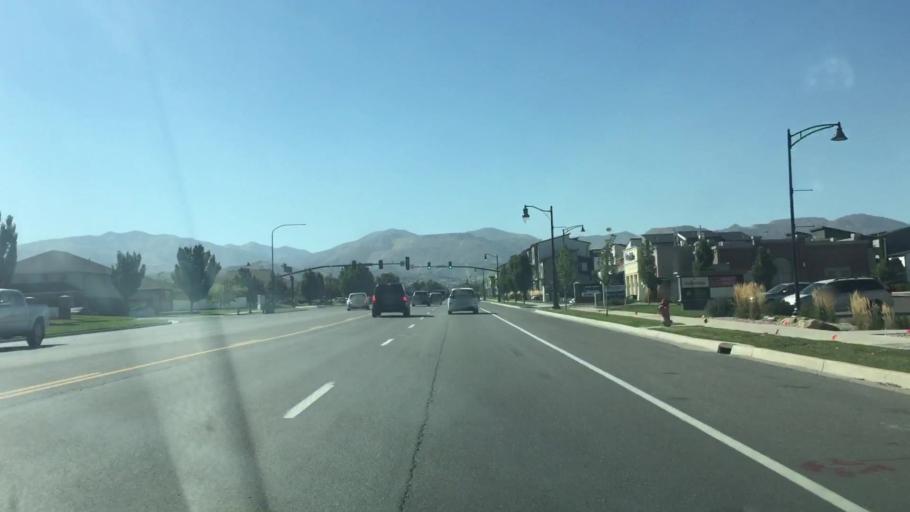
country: US
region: Utah
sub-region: Salt Lake County
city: Herriman
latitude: 40.5080
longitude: -112.0129
